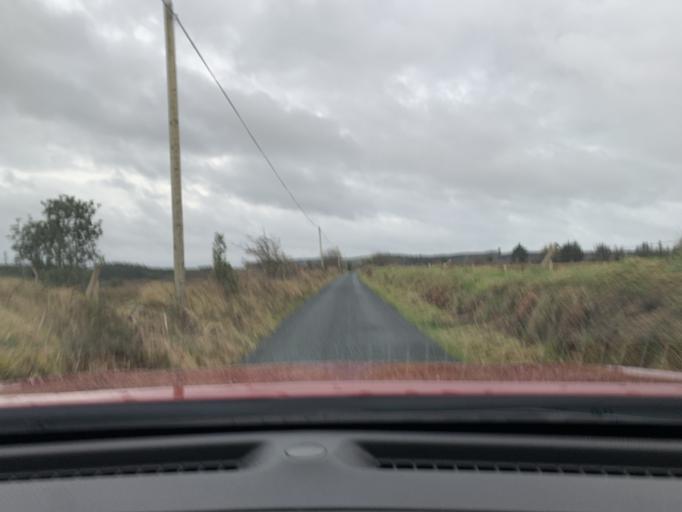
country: IE
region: Connaught
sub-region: Roscommon
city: Ballaghaderreen
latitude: 53.9701
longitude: -8.5255
